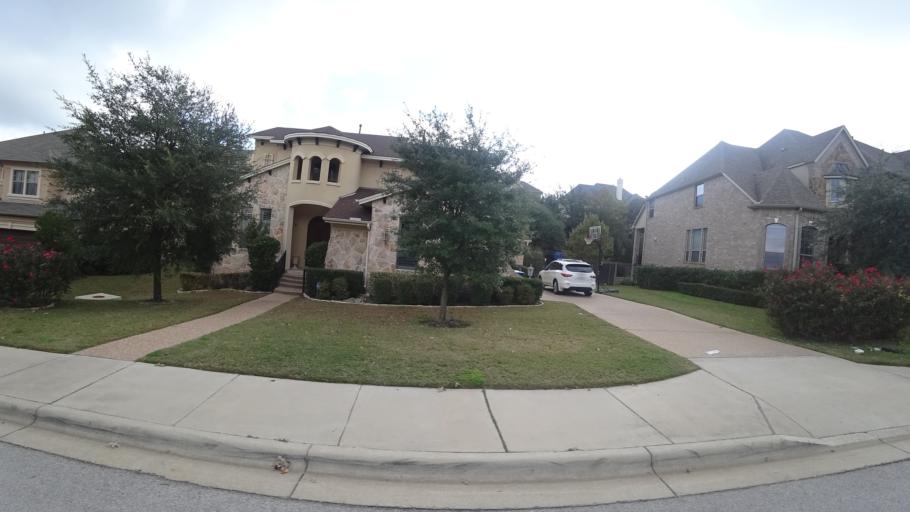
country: US
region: Texas
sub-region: Travis County
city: Barton Creek
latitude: 30.3146
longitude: -97.8976
